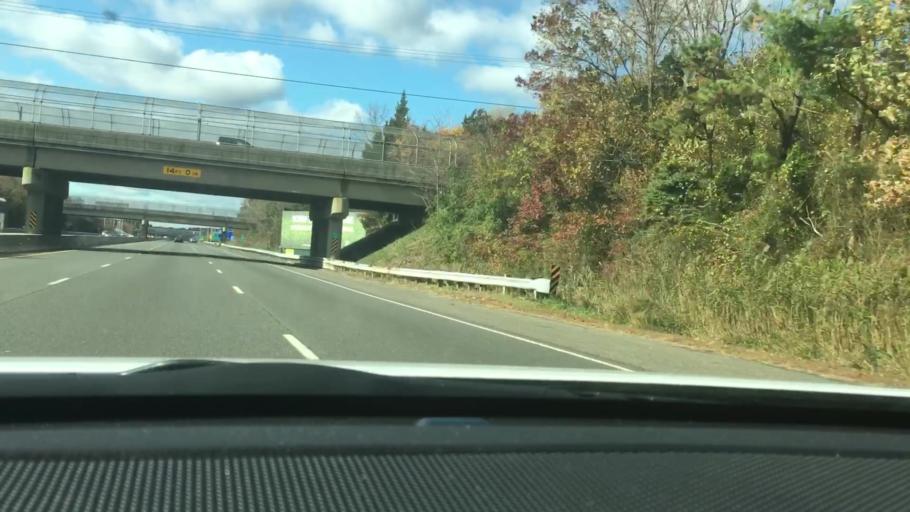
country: US
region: New Jersey
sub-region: Atlantic County
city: Pleasantville
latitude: 39.3981
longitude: -74.5163
